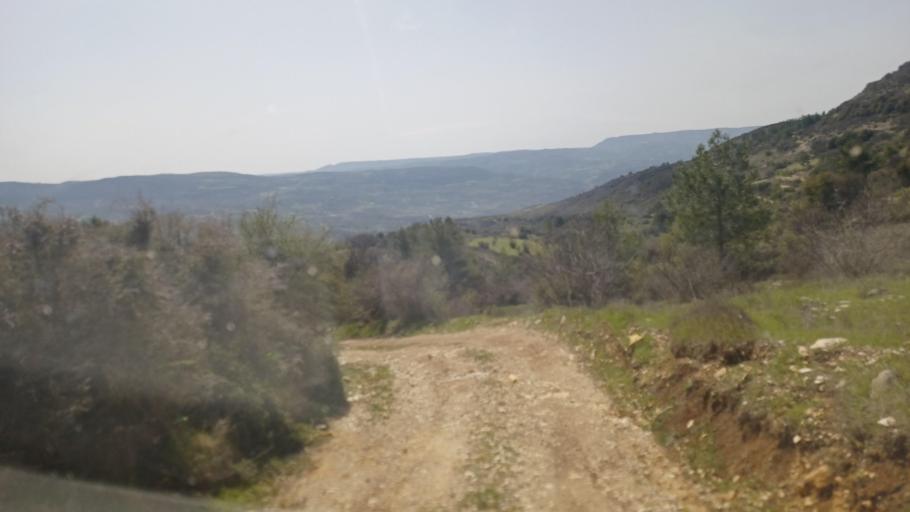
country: CY
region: Limassol
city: Pachna
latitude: 34.8734
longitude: 32.7055
